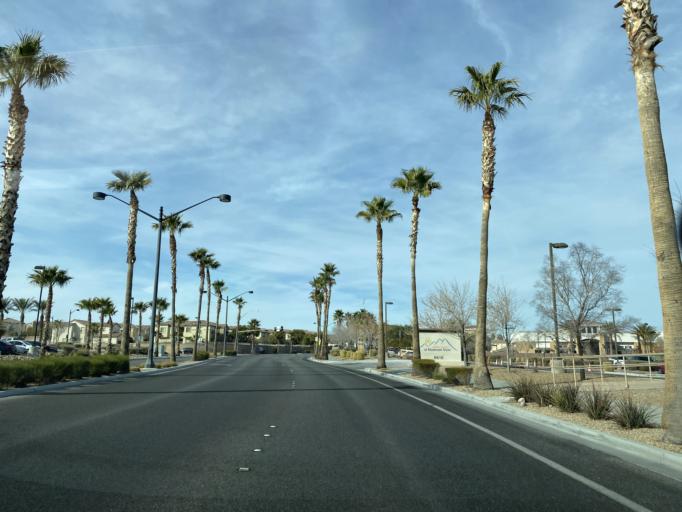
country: US
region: Nevada
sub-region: Clark County
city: Summerlin South
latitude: 36.2807
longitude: -115.2795
